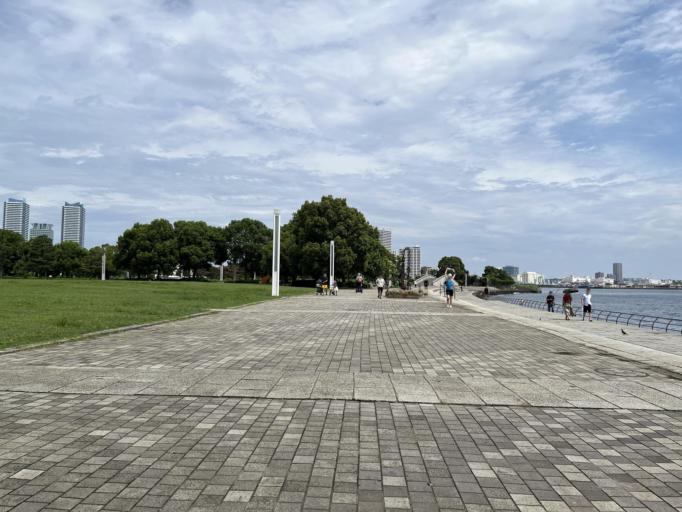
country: JP
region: Kanagawa
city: Yokohama
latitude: 35.4605
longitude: 139.6378
